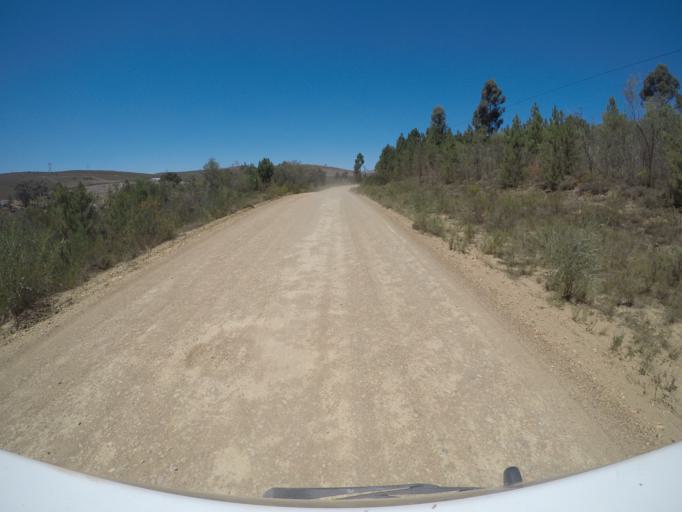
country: ZA
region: Western Cape
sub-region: Overberg District Municipality
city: Caledon
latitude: -34.1862
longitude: 19.2238
